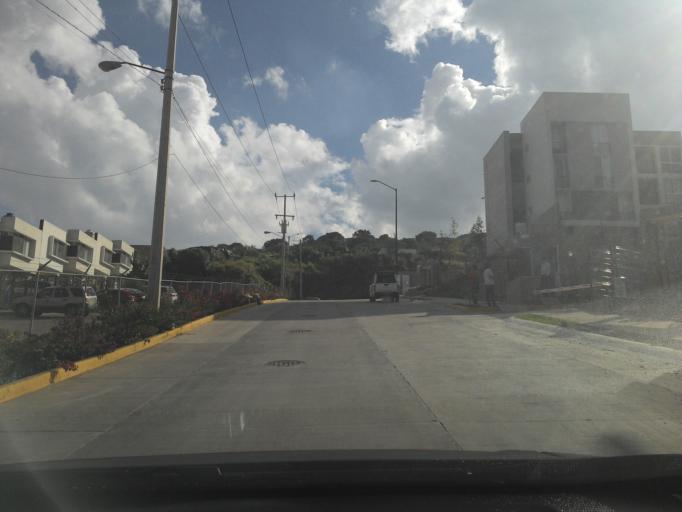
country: MX
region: Jalisco
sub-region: Tlajomulco de Zuniga
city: Altus Bosques
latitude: 20.6072
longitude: -103.3609
